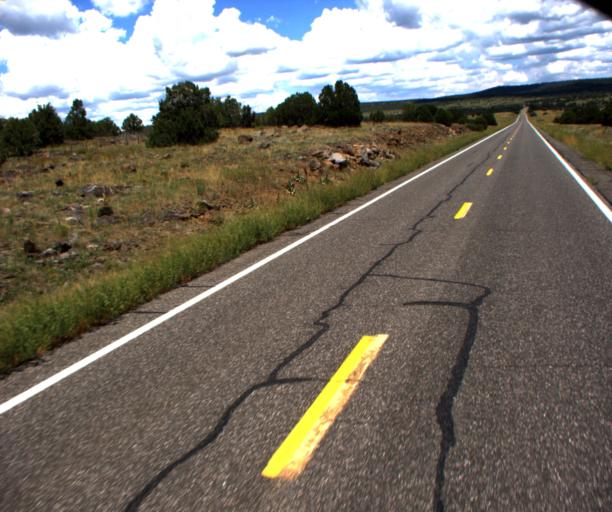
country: US
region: Arizona
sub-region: Gila County
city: Pine
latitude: 34.4943
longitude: -111.5900
